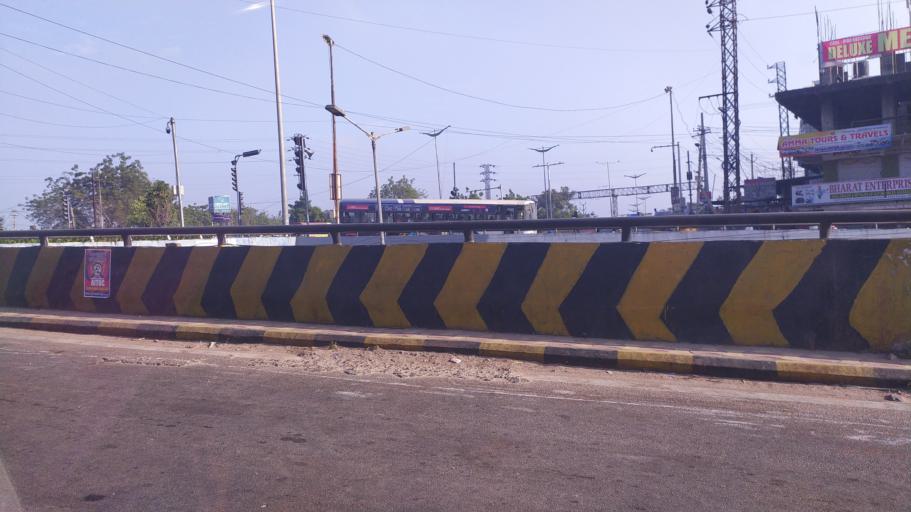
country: IN
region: Telangana
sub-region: Hyderabad
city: Hyderabad
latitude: 17.3214
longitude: 78.4323
